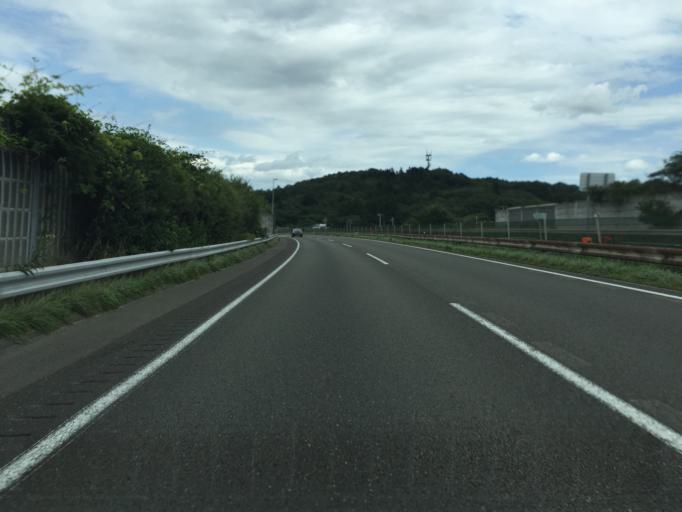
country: JP
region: Miyagi
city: Sendai
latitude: 38.1932
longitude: 140.7829
